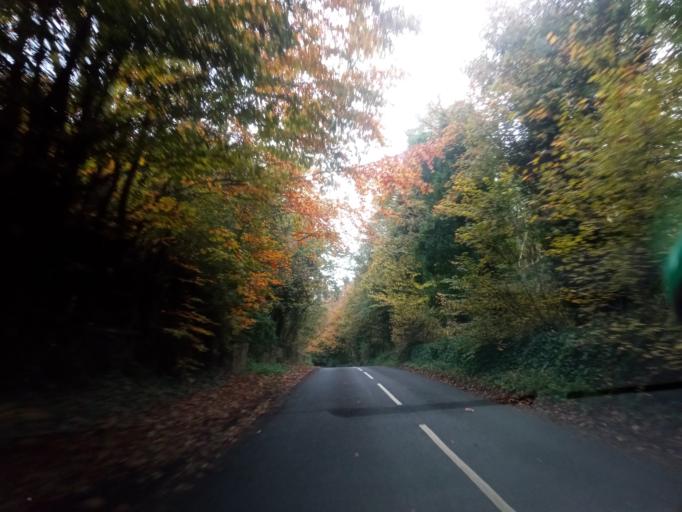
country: GB
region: Scotland
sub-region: The Scottish Borders
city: Eyemouth
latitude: 55.8487
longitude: -2.1127
